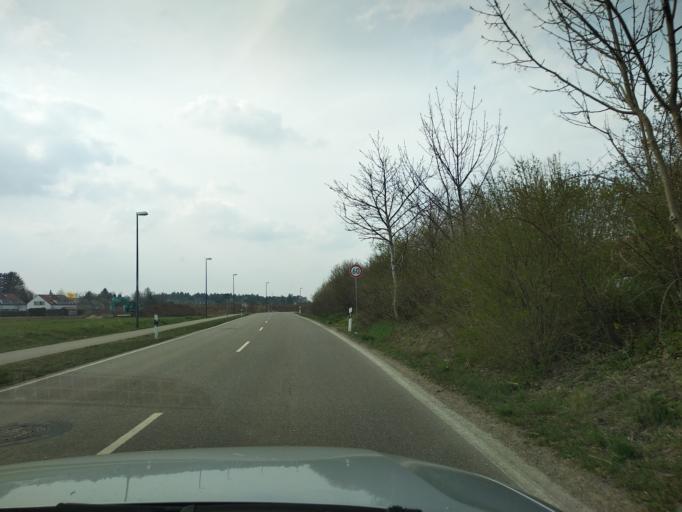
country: DE
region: Bavaria
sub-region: Upper Bavaria
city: Vaterstetten
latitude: 48.1137
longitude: 11.7761
